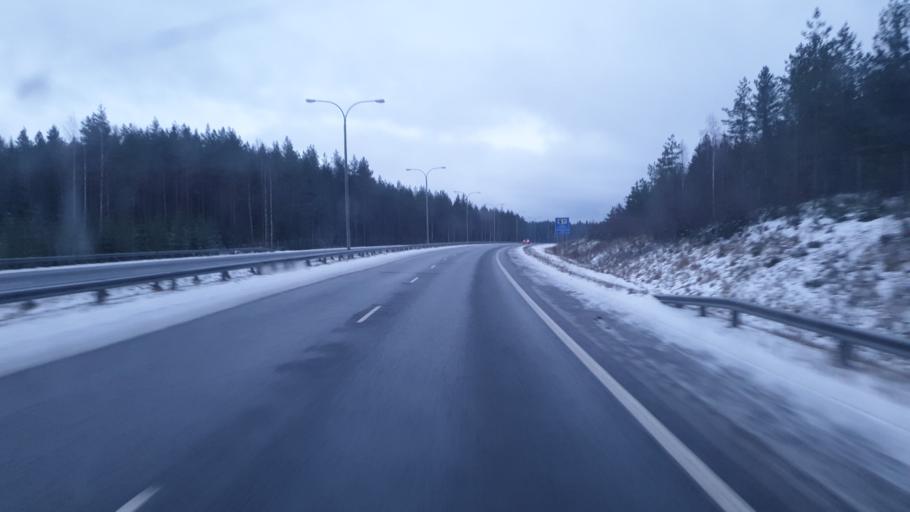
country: FI
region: Northern Savo
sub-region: Kuopio
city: Siilinjaervi
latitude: 63.0101
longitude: 27.6784
